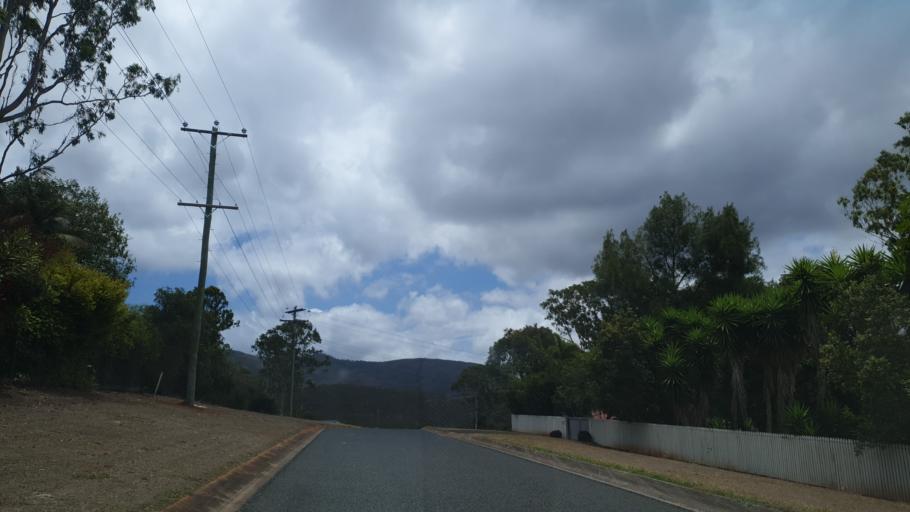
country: AU
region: Queensland
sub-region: Tablelands
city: Tolga
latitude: -17.2099
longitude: 145.4453
